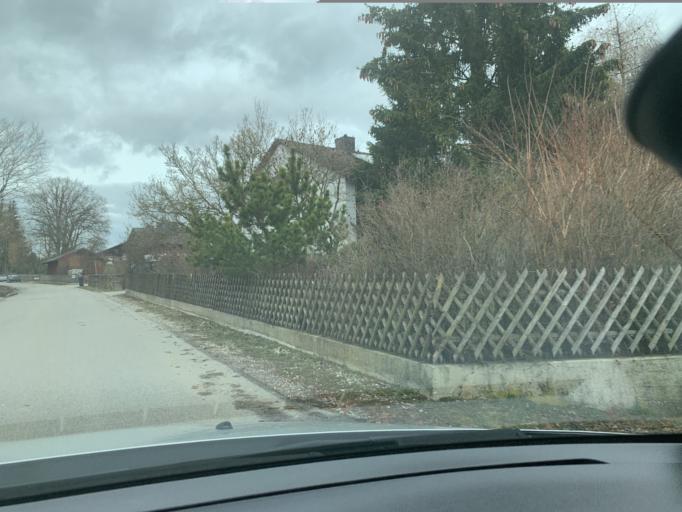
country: DE
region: Bavaria
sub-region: Lower Bavaria
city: Eging
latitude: 48.4932
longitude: 12.2000
